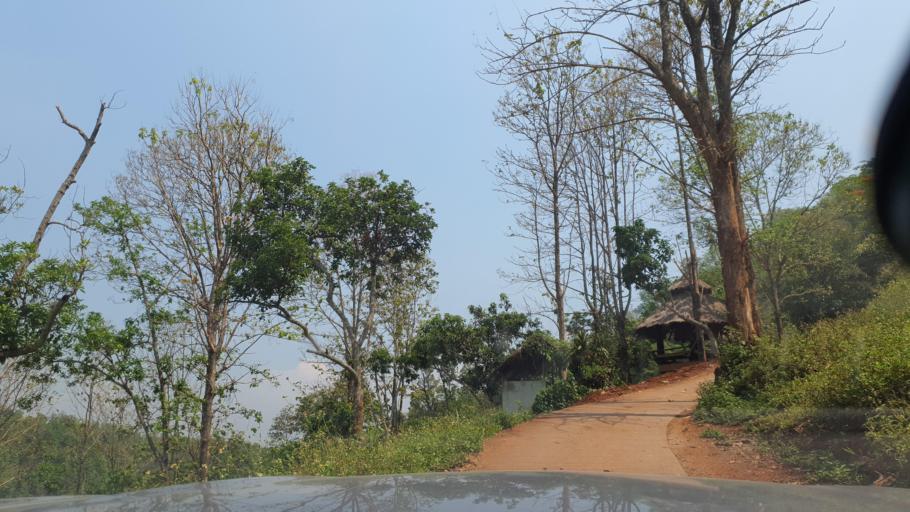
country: TH
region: Chiang Mai
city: Samoeng
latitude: 18.8052
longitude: 98.8188
